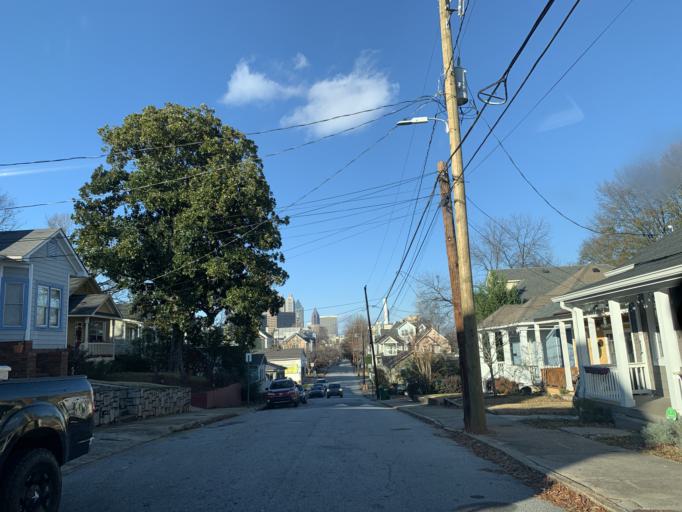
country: US
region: Georgia
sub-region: Fulton County
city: Atlanta
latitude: 33.7384
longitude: -84.3841
